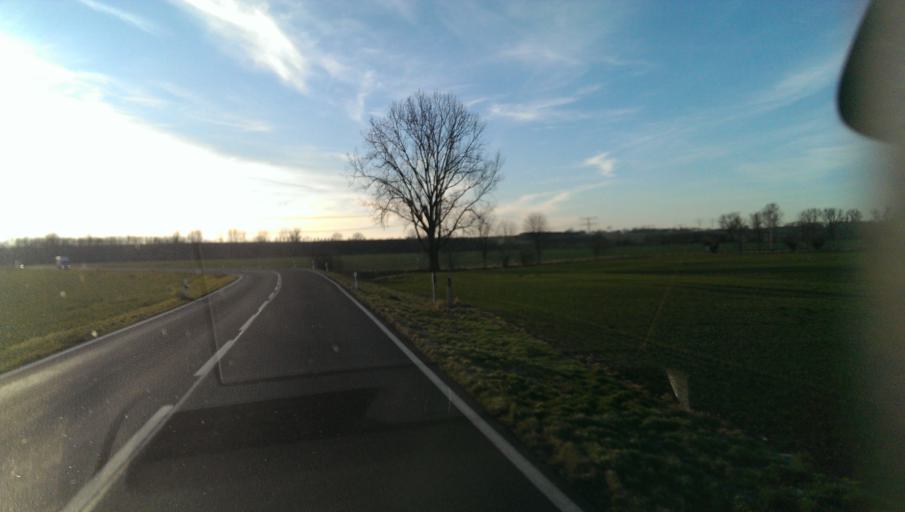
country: DE
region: Saxony-Anhalt
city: Eilsleben
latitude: 52.1737
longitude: 11.2449
